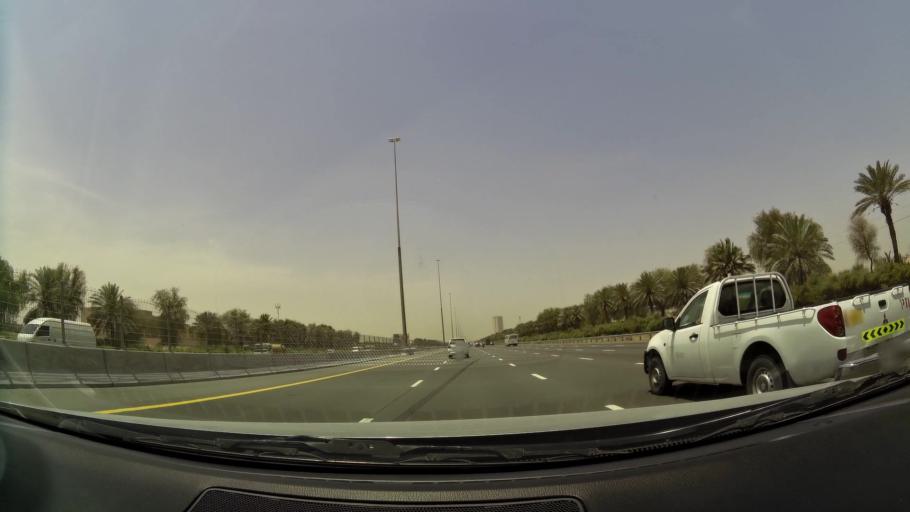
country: AE
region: Dubai
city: Dubai
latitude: 25.1054
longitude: 55.3392
